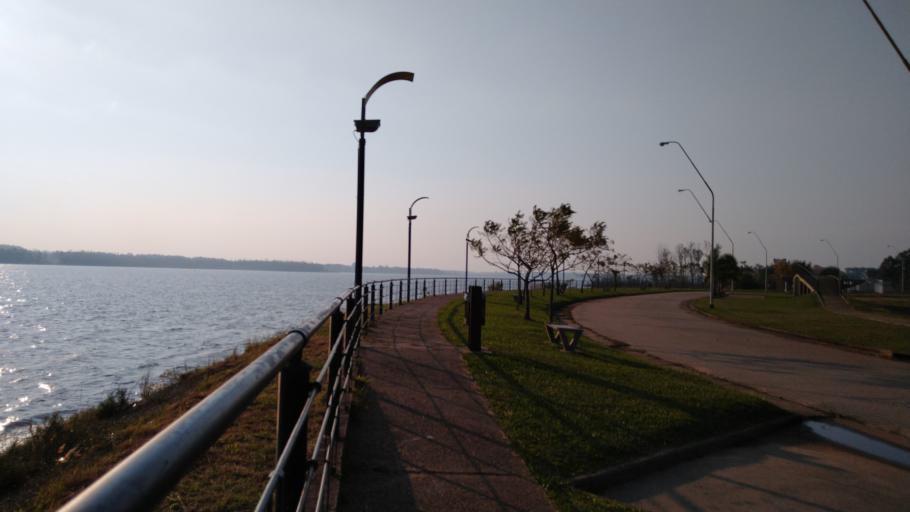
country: AR
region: Entre Rios
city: Santa Ana
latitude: -30.8992
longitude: -57.9366
